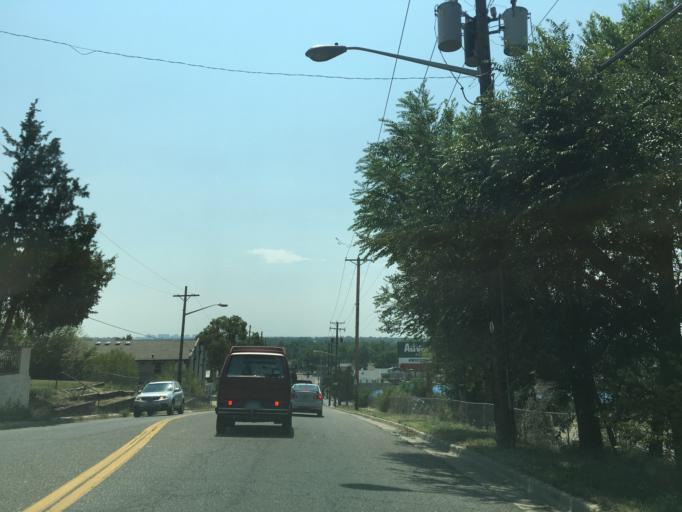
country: US
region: Colorado
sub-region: Arapahoe County
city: Glendale
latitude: 39.7087
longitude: -104.9223
